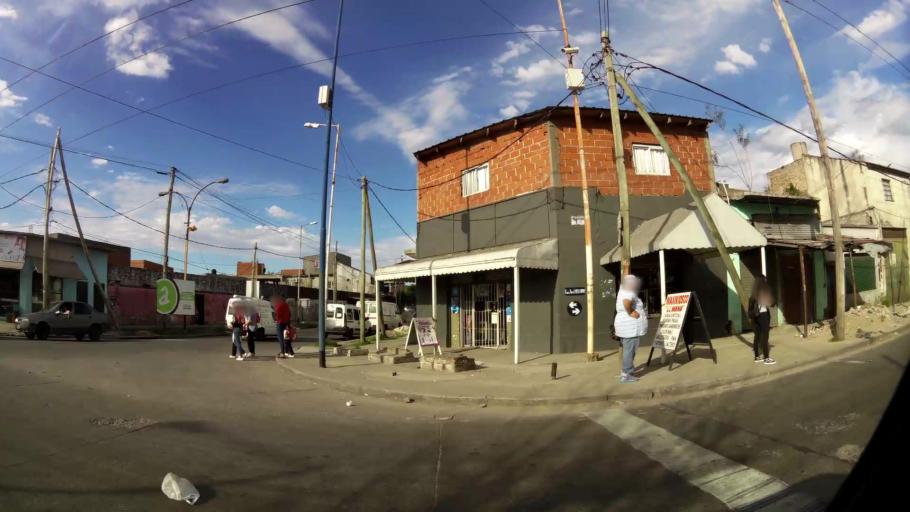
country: AR
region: Buenos Aires
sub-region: Partido de Lanus
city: Lanus
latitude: -34.7045
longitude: -58.3596
